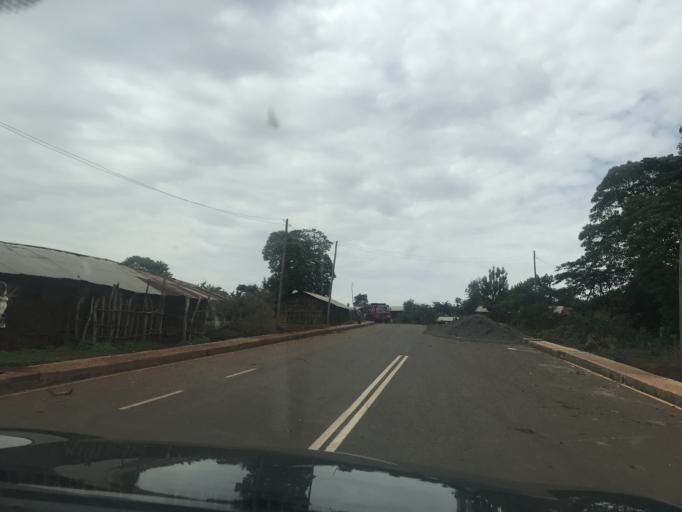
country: ET
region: Oromiya
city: Shambu
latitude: 9.8683
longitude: 36.6840
